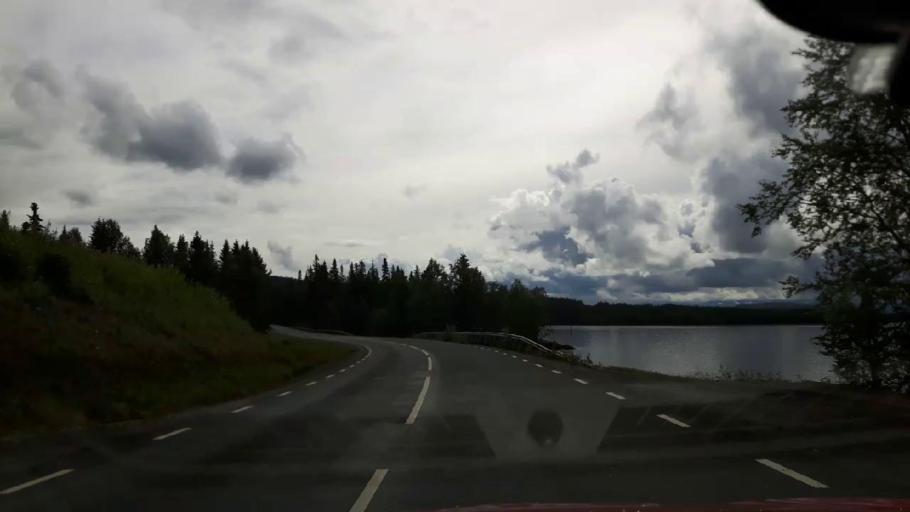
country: NO
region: Nord-Trondelag
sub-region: Lierne
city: Sandvika
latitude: 64.6493
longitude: 14.1384
